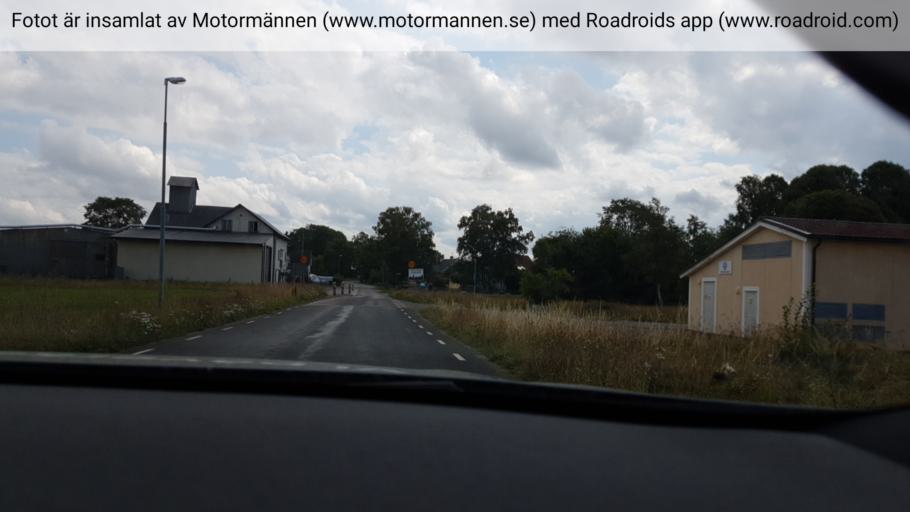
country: SE
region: Vaestra Goetaland
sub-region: Falkopings Kommun
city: Falkoeping
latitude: 58.0888
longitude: 13.5169
